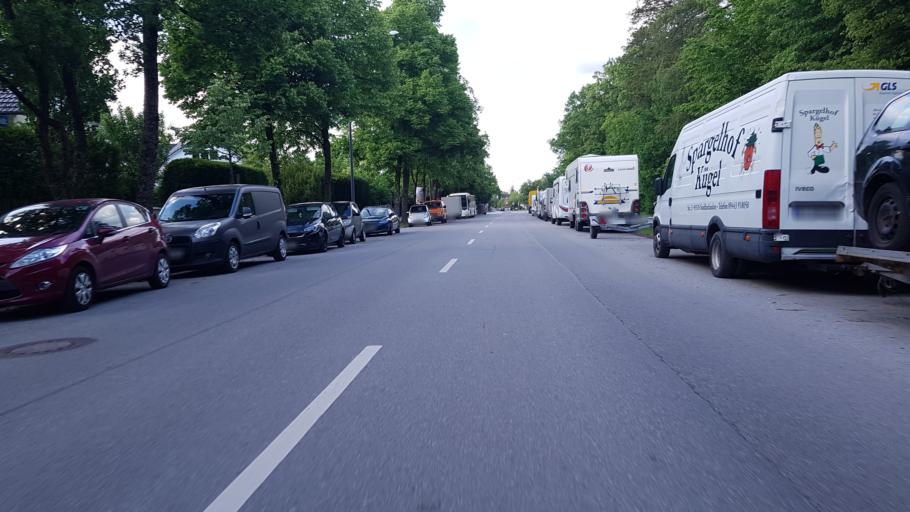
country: DE
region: Bavaria
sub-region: Upper Bavaria
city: Neuried
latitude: 48.1105
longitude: 11.4930
